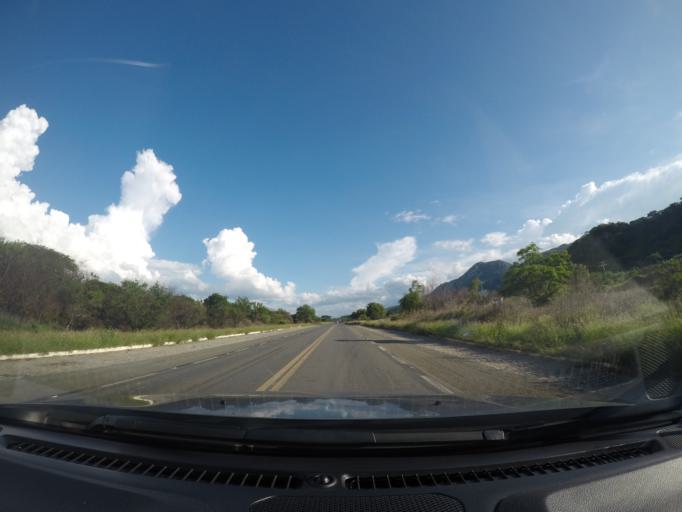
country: BR
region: Bahia
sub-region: Oliveira Dos Brejinhos
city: Oliveira dos Brejinhos
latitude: -12.0553
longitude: -42.9654
